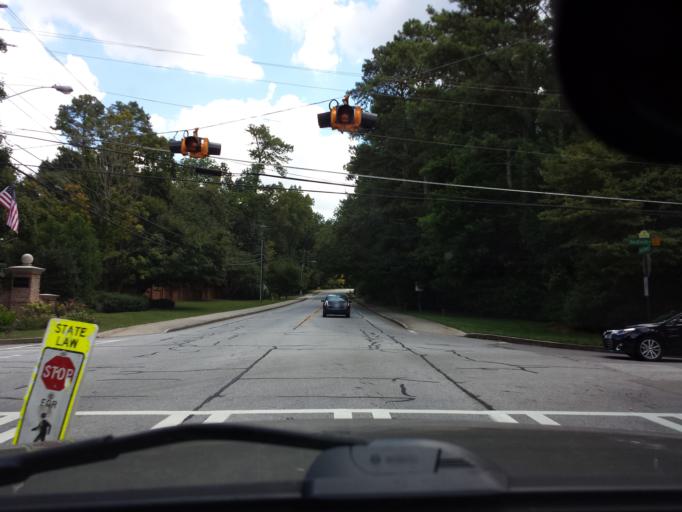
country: US
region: Georgia
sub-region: DeKalb County
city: Dunwoody
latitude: 33.9589
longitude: -84.3436
